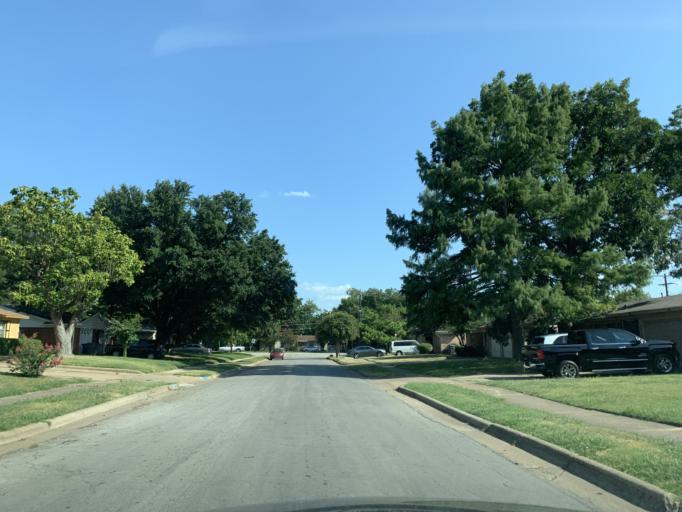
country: US
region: Texas
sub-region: Dallas County
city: Hutchins
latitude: 32.6884
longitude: -96.7873
